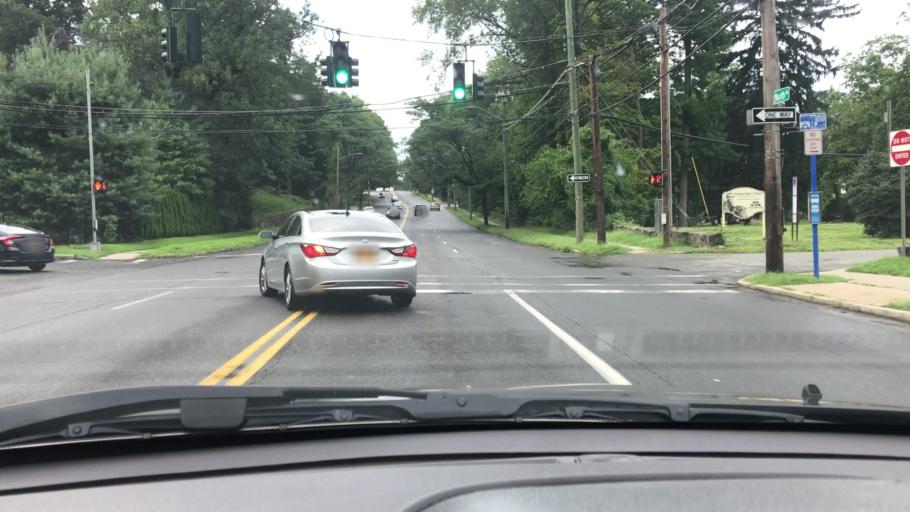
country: US
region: New York
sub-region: Westchester County
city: New Rochelle
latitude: 40.9328
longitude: -73.7912
